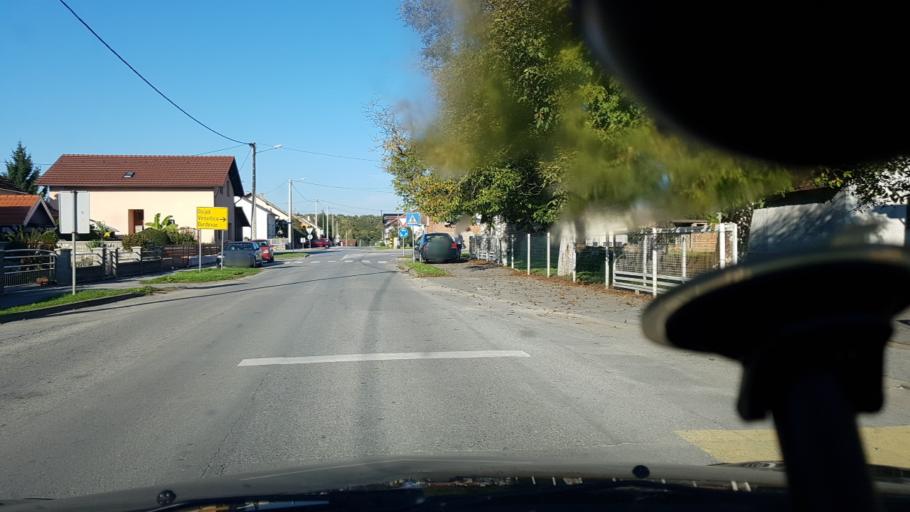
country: HR
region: Bjelovarsko-Bilogorska
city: Bjelovar
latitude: 45.9205
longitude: 16.8616
